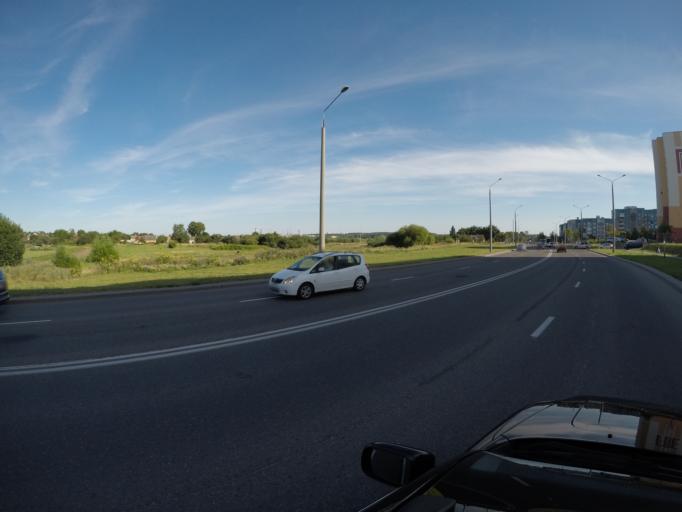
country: BY
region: Grodnenskaya
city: Hrodna
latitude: 53.7068
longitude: 23.8591
